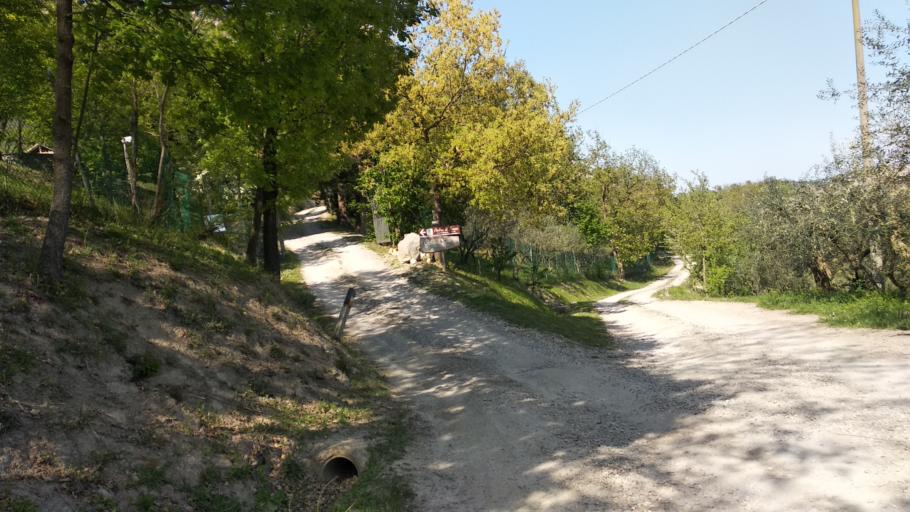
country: IT
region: Emilia-Romagna
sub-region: Provincia di Ravenna
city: Fognano
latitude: 44.2359
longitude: 11.7101
